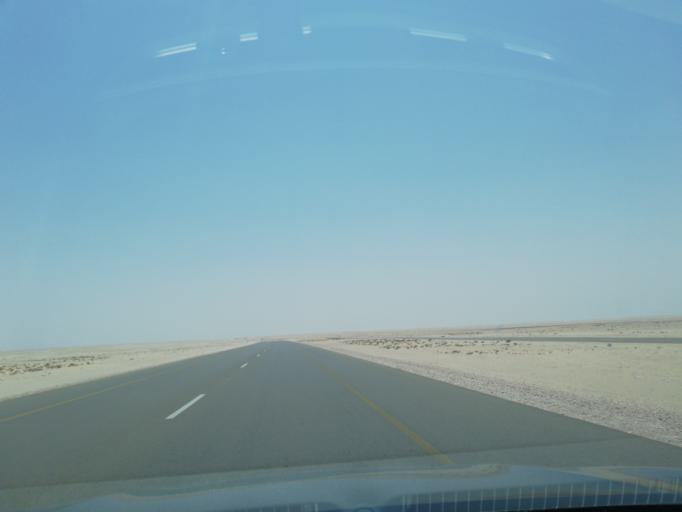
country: OM
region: Al Wusta
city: Hayma'
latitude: 19.7855
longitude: 56.1182
